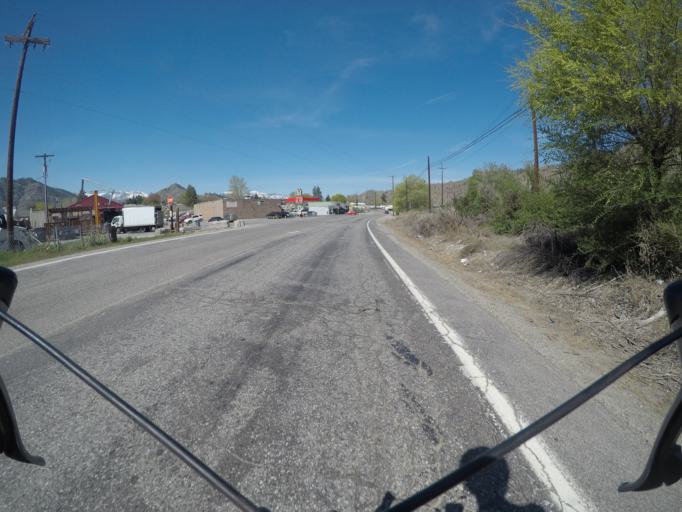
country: US
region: Washington
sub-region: Chelan County
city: Cashmere
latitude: 47.5227
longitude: -120.4826
